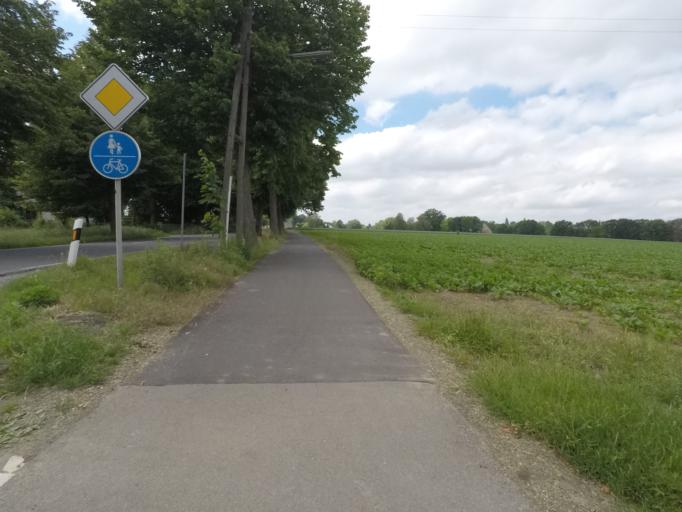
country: DE
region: North Rhine-Westphalia
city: Enger
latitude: 52.1320
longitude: 8.5226
